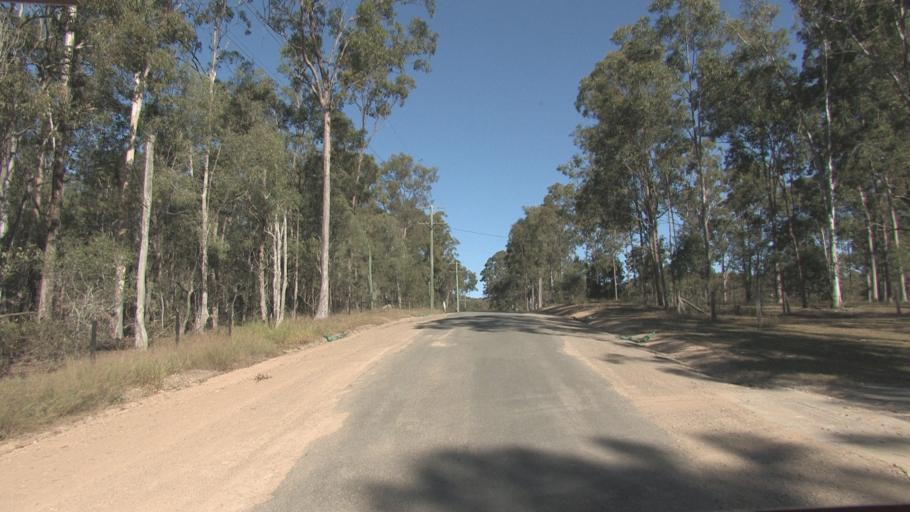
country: AU
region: Queensland
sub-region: Logan
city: Windaroo
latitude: -27.7586
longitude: 153.1509
